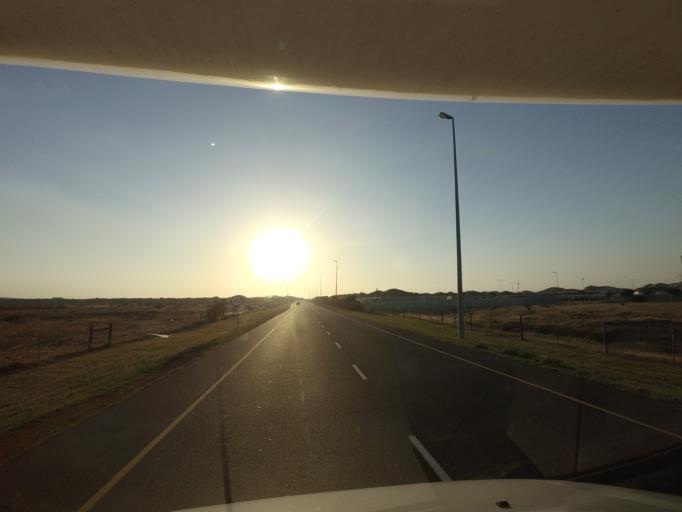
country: ZA
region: Western Cape
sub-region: City of Cape Town
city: Sunset Beach
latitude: -33.7263
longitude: 18.4537
